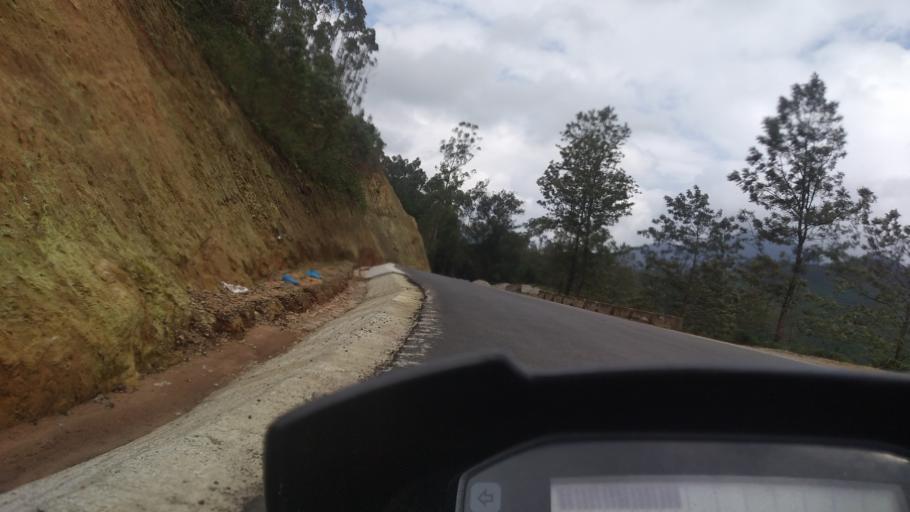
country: IN
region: Kerala
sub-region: Idukki
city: Munnar
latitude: 10.0749
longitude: 77.0897
